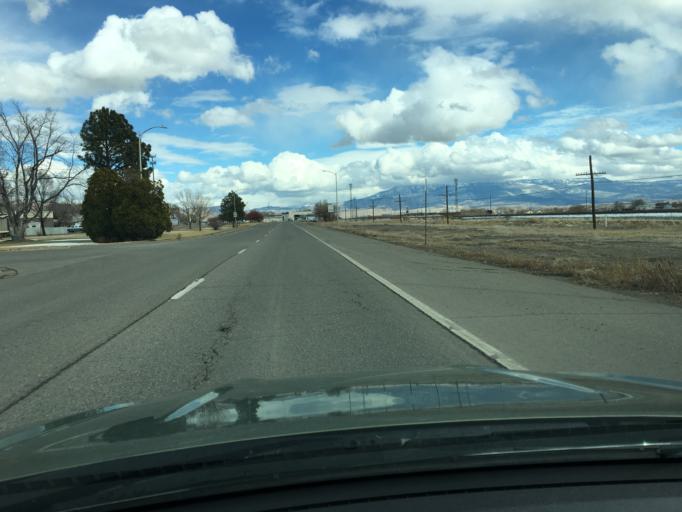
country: US
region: Colorado
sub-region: Mesa County
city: Grand Junction
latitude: 39.0646
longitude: -108.5494
